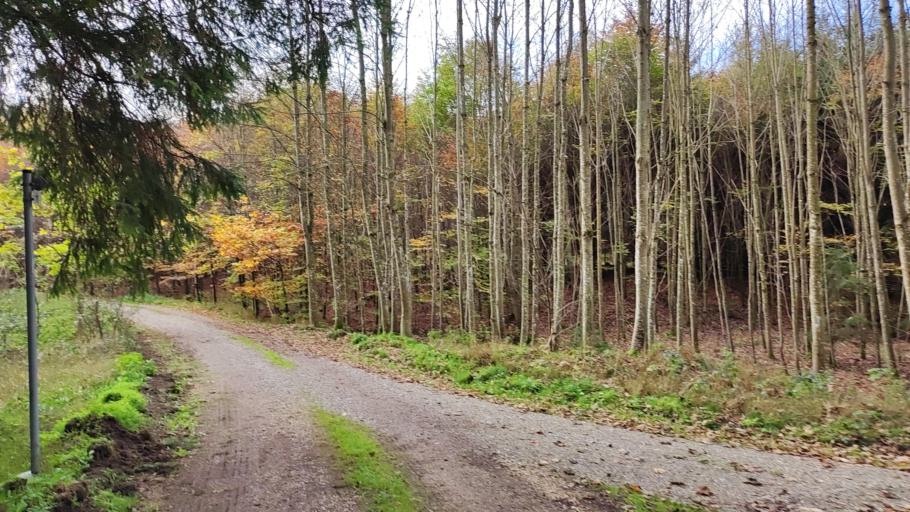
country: DE
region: Bavaria
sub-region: Swabia
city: Munsterhausen
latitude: 48.3264
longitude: 10.4871
